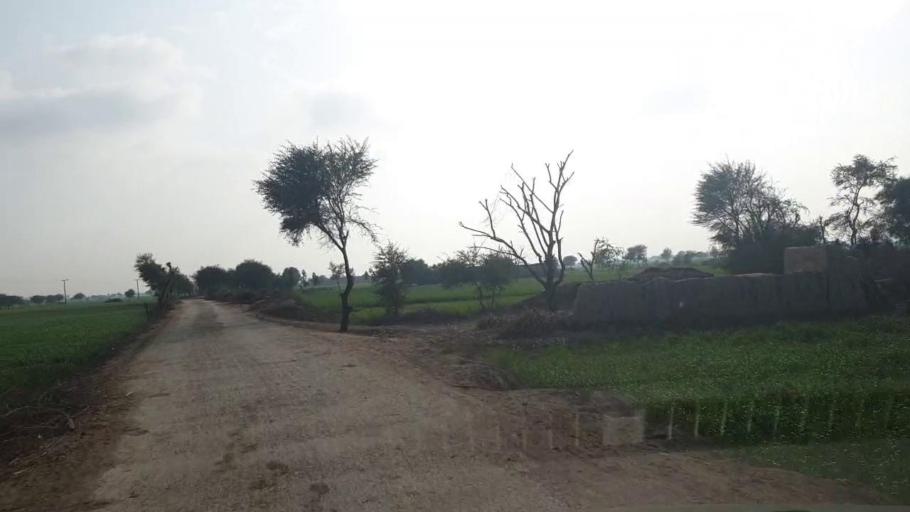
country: PK
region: Sindh
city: Shahdadpur
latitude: 25.8812
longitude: 68.6665
